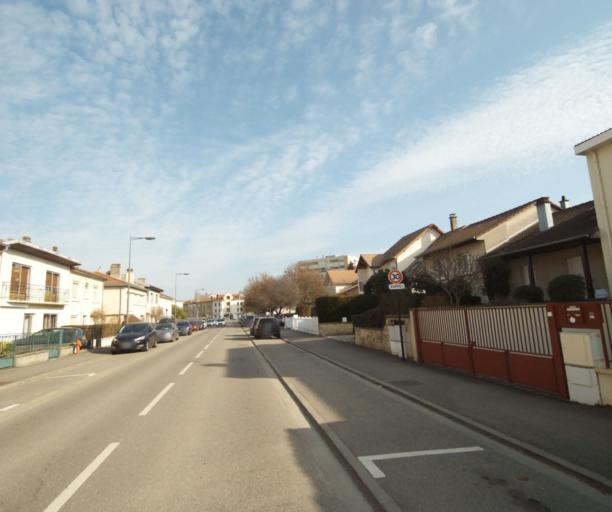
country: FR
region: Lorraine
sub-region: Departement de Meurthe-et-Moselle
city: Villers-les-Nancy
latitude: 48.6758
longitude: 6.1557
